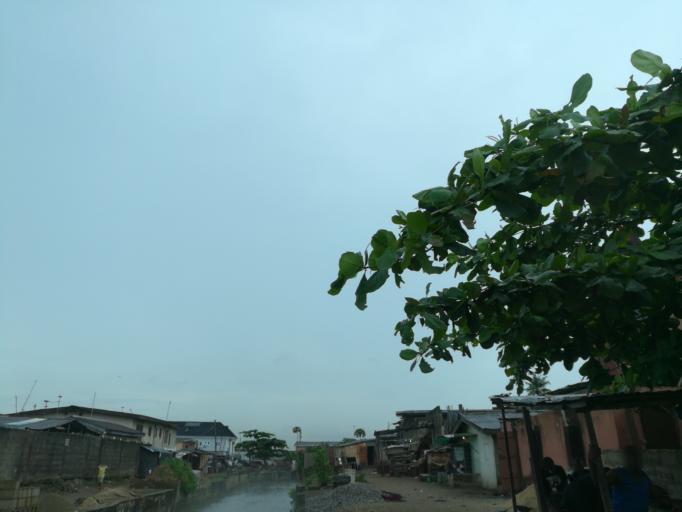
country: NG
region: Lagos
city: Oshodi
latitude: 6.5611
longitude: 3.3388
